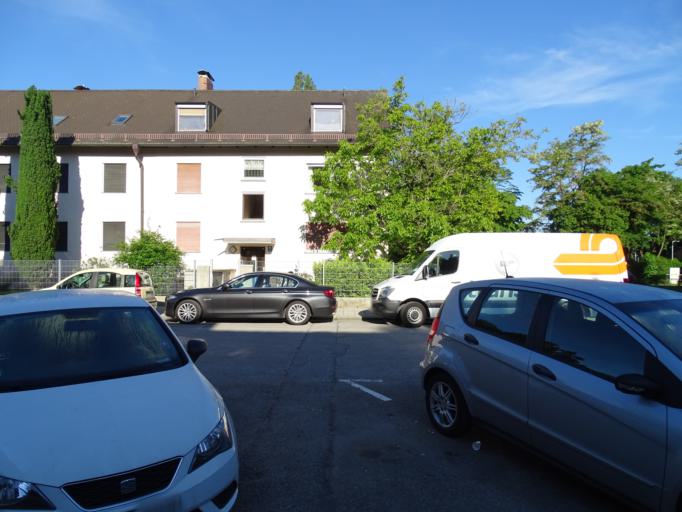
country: DE
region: Bavaria
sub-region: Upper Bavaria
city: Oberschleissheim
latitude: 48.2077
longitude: 11.5718
